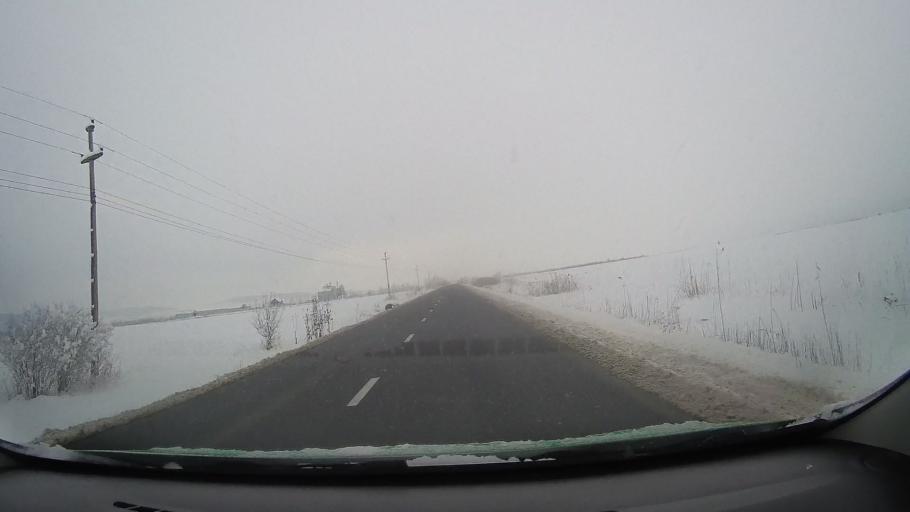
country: RO
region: Sibiu
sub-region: Comuna Cristian
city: Cristian
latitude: 45.7667
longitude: 24.0044
